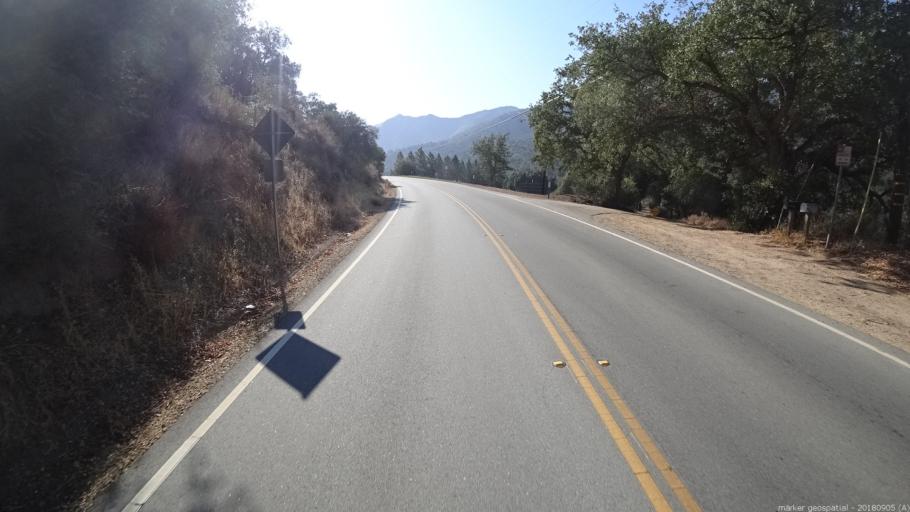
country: US
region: California
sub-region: Monterey County
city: Soledad
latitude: 36.2322
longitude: -121.4671
